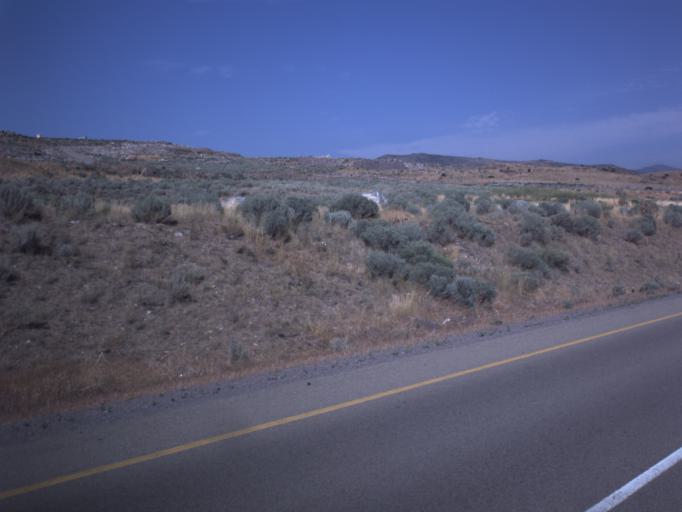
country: US
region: Utah
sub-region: Salt Lake County
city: Bluffdale
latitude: 40.4660
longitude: -111.9576
